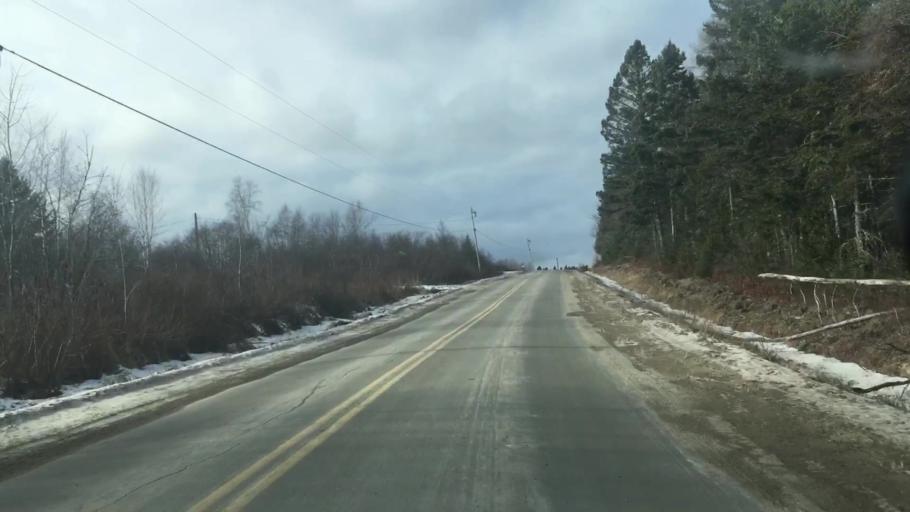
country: US
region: Maine
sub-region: Washington County
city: Machias
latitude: 44.6563
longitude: -67.5307
